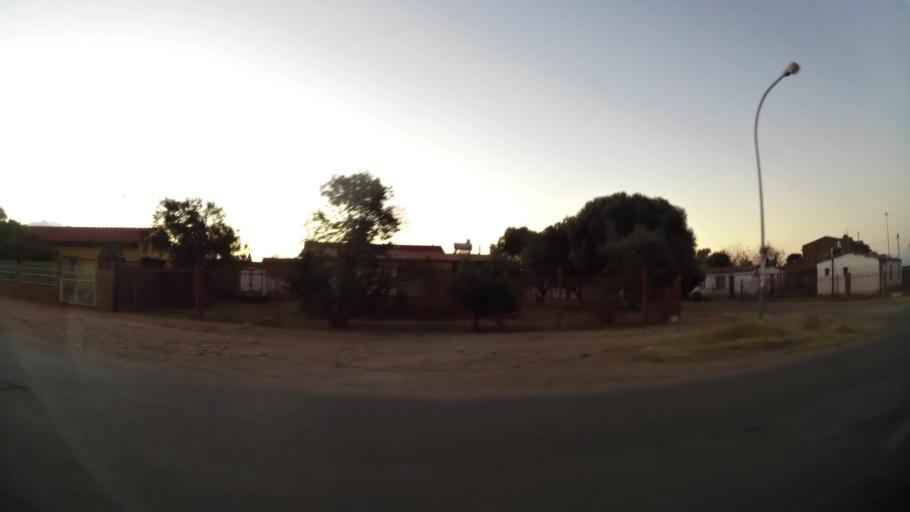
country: ZA
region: Northern Cape
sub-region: Frances Baard District Municipality
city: Kimberley
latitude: -28.7235
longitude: 24.7646
